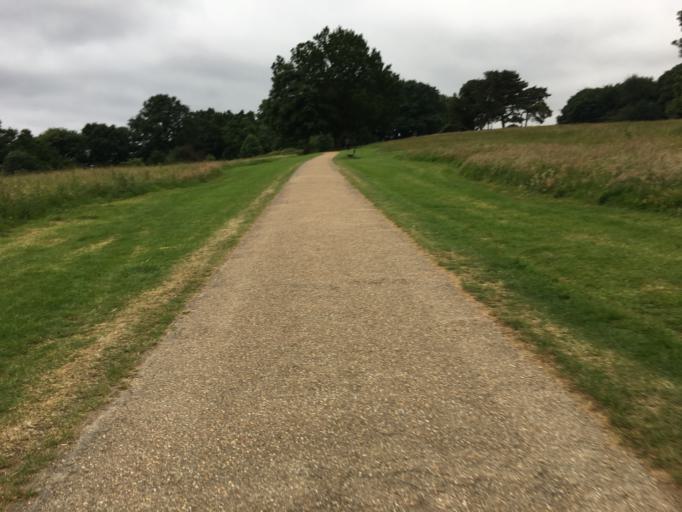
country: GB
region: England
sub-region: Greater London
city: Belsize Park
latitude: 51.5627
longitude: -0.1591
